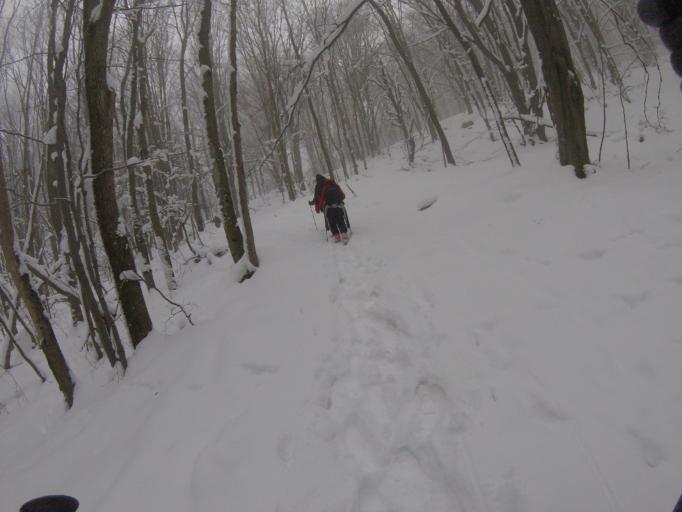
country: HU
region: Heves
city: Belapatfalva
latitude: 48.0455
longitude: 20.3965
